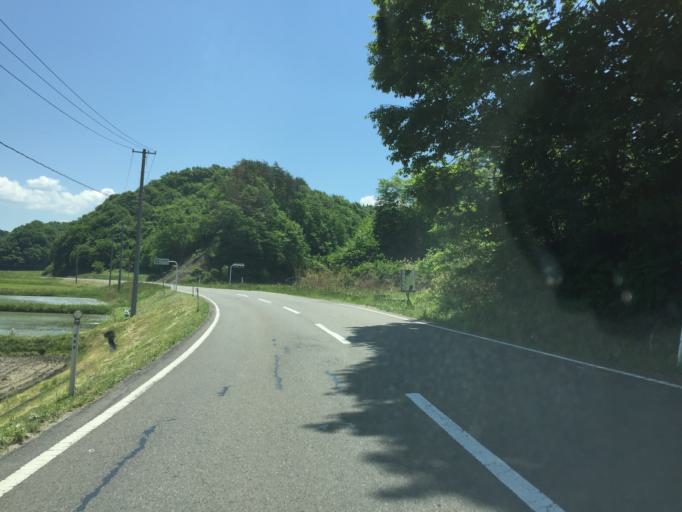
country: JP
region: Fukushima
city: Miharu
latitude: 37.4931
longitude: 140.5084
